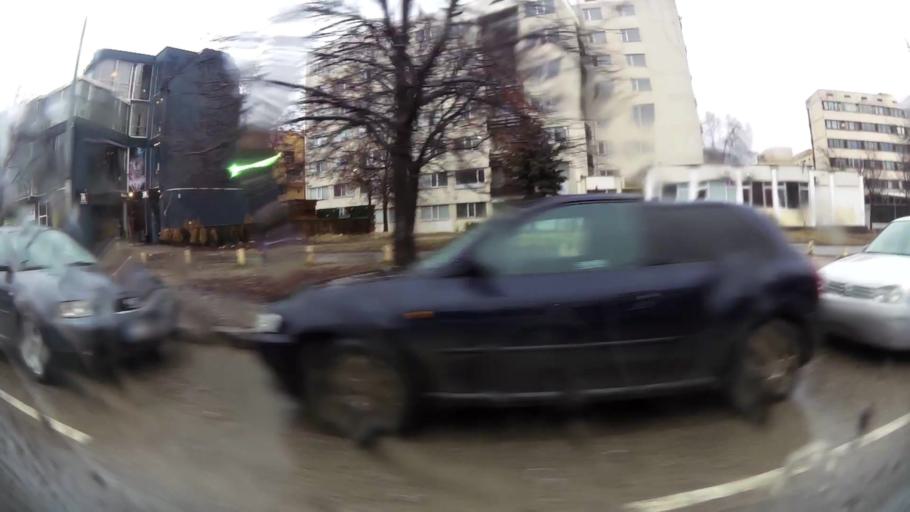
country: BG
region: Sofia-Capital
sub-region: Stolichna Obshtina
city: Sofia
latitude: 42.6515
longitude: 23.3433
